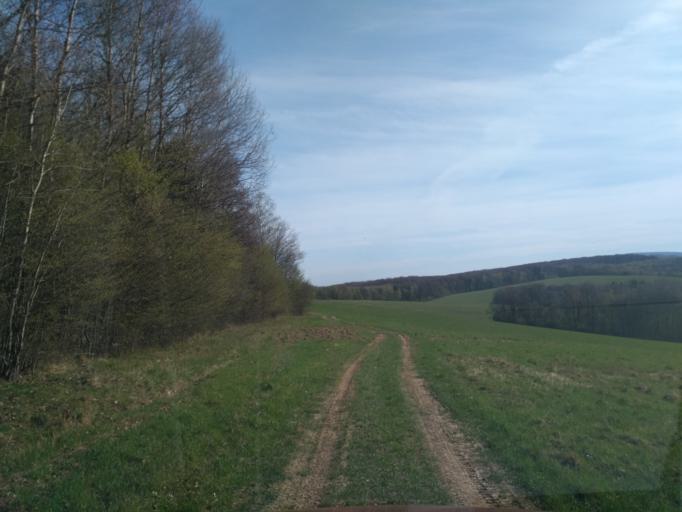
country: SK
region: Presovsky
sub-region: Okres Presov
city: Presov
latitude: 48.9257
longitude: 21.2187
